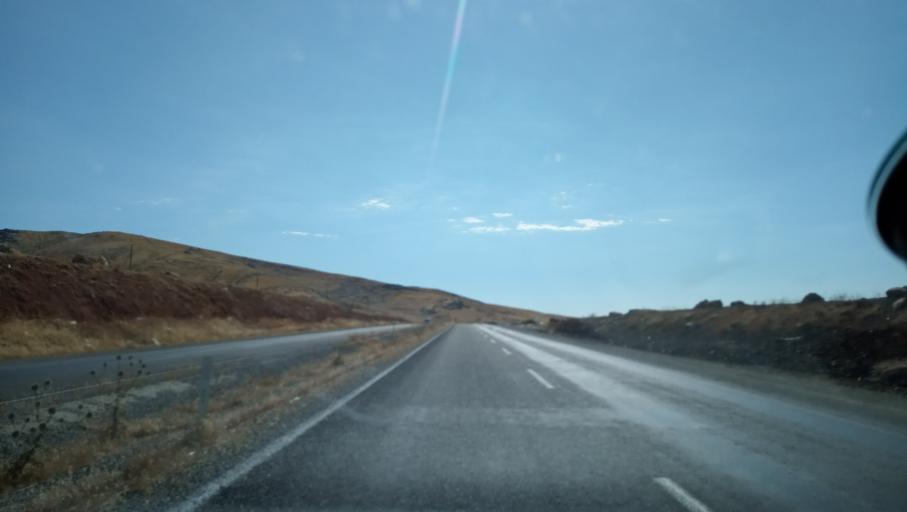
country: TR
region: Diyarbakir
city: Silvan
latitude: 38.1278
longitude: 41.0824
